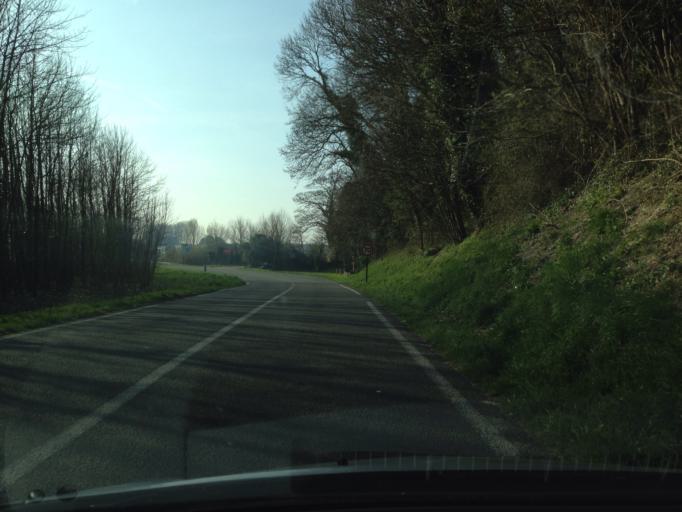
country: FR
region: Nord-Pas-de-Calais
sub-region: Departement du Pas-de-Calais
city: Saint-Josse
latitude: 50.5061
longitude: 1.6703
